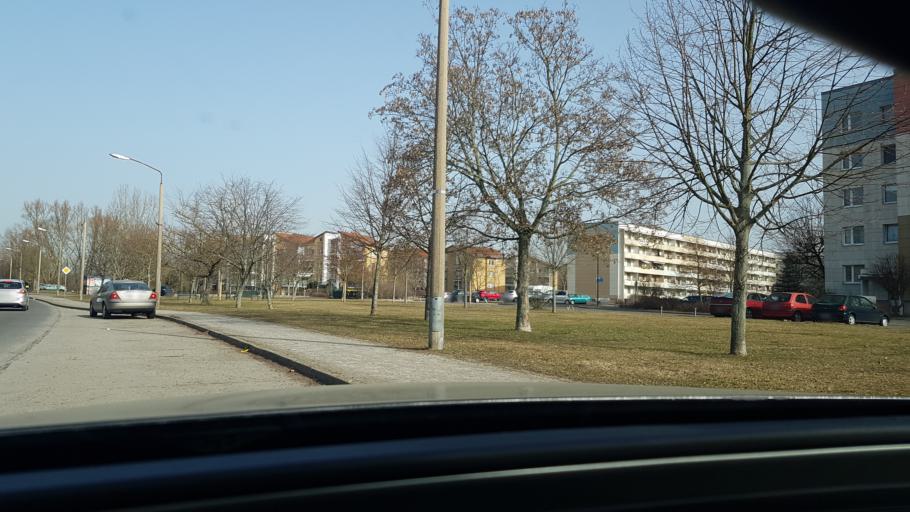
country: DE
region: Brandenburg
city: Peitz
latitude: 51.8571
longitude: 14.4191
